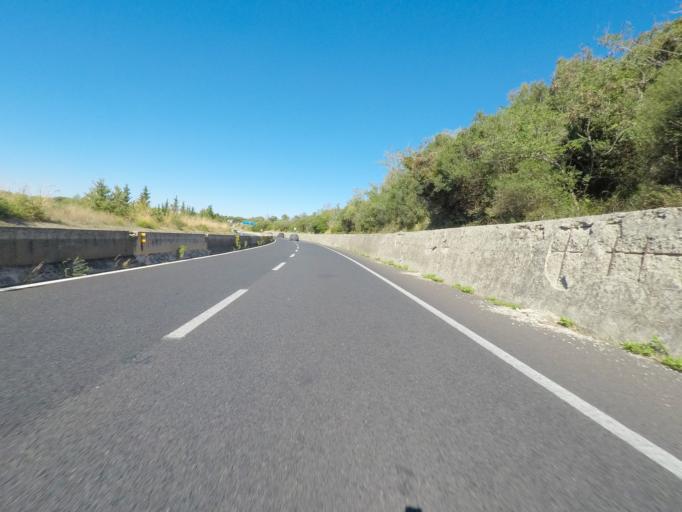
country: IT
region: Tuscany
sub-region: Provincia di Grosseto
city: Fonteblanda
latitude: 42.5627
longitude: 11.1735
